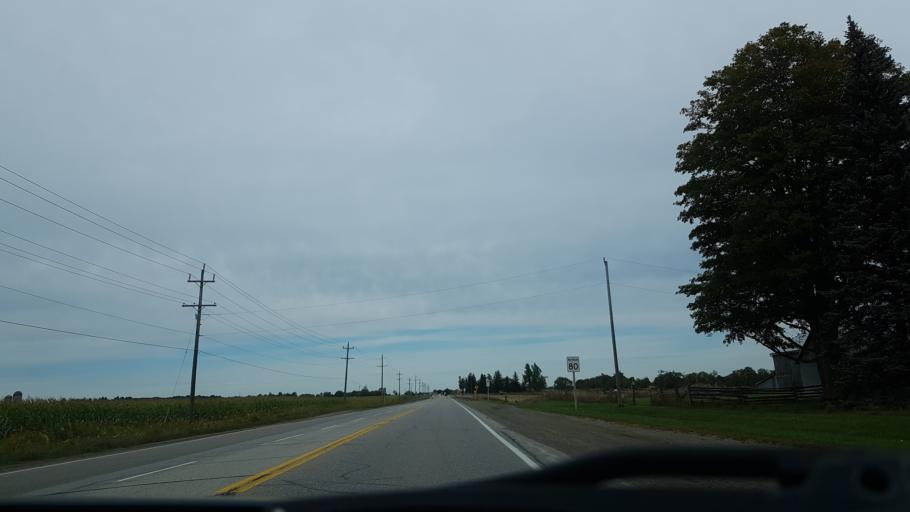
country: CA
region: Ontario
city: Orangeville
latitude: 43.8174
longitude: -80.0432
